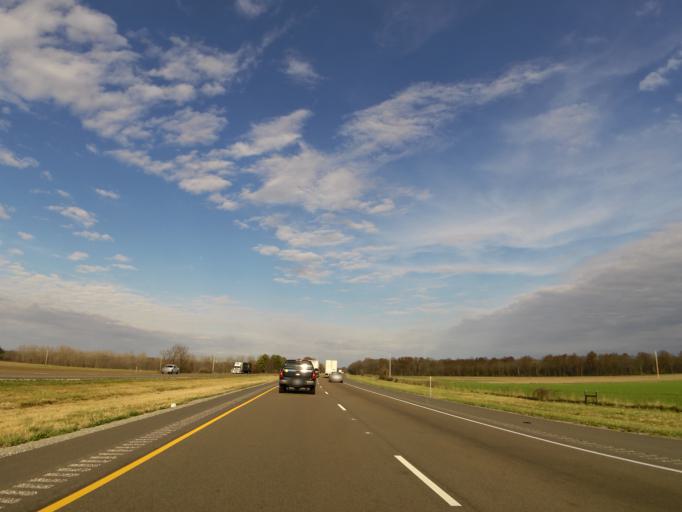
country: US
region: Illinois
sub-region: Washington County
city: Okawville
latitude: 38.4611
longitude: -89.5679
